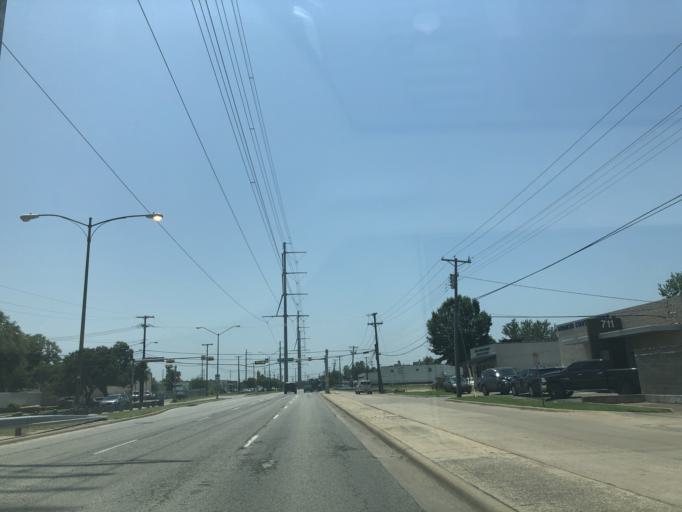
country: US
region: Texas
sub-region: Dallas County
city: Dallas
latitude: 32.8039
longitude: -96.8443
